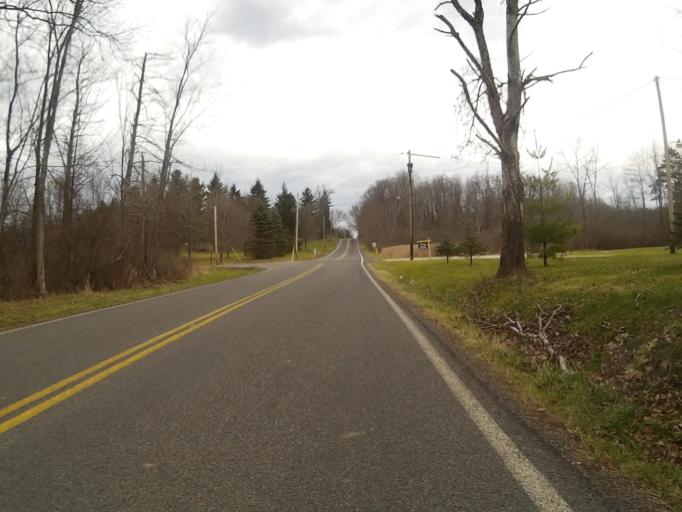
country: US
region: Ohio
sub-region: Portage County
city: Brimfield
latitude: 41.0648
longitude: -81.3287
